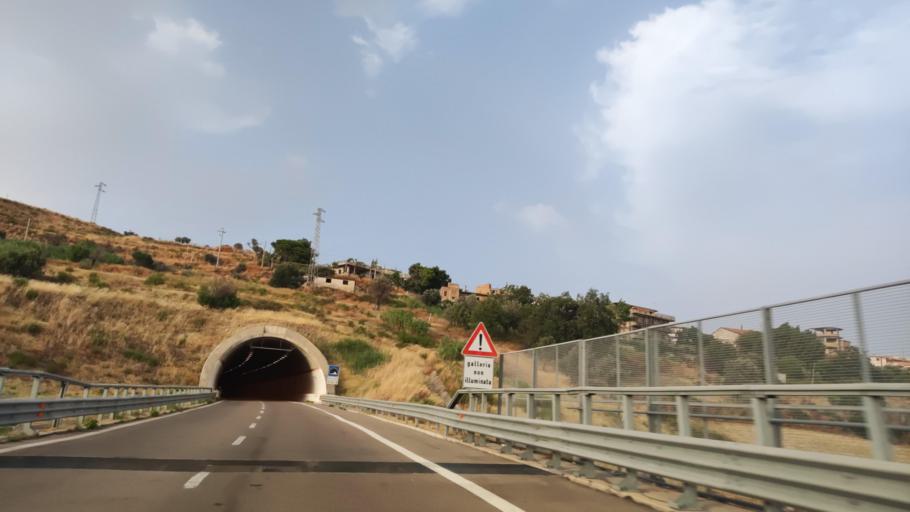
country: IT
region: Calabria
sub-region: Provincia di Reggio Calabria
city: Siderno
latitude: 38.2935
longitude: 16.2853
